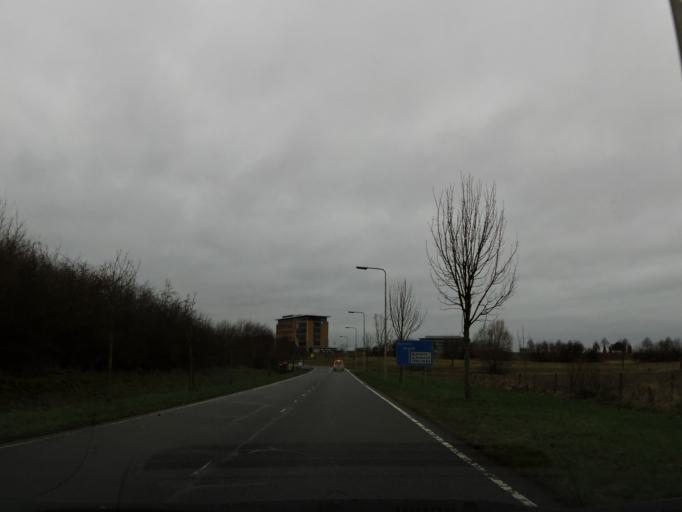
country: NL
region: Limburg
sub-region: Gemeente Simpelveld
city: Simpelveld
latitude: 50.8251
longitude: 6.0217
